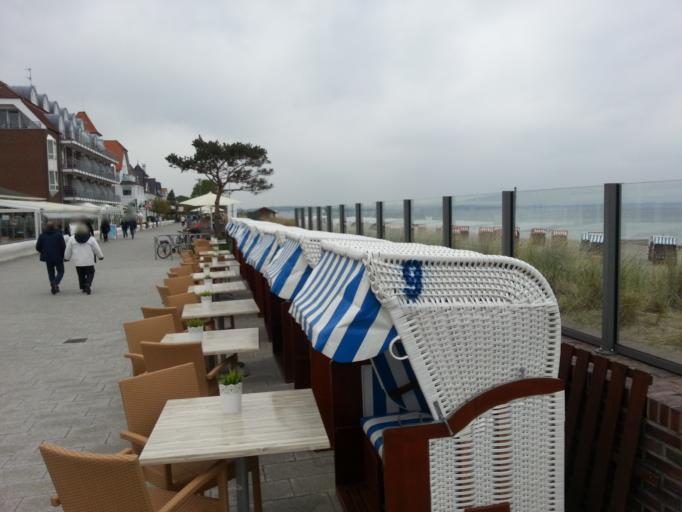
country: DE
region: Schleswig-Holstein
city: Timmendorfer Strand
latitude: 53.9928
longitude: 10.8284
